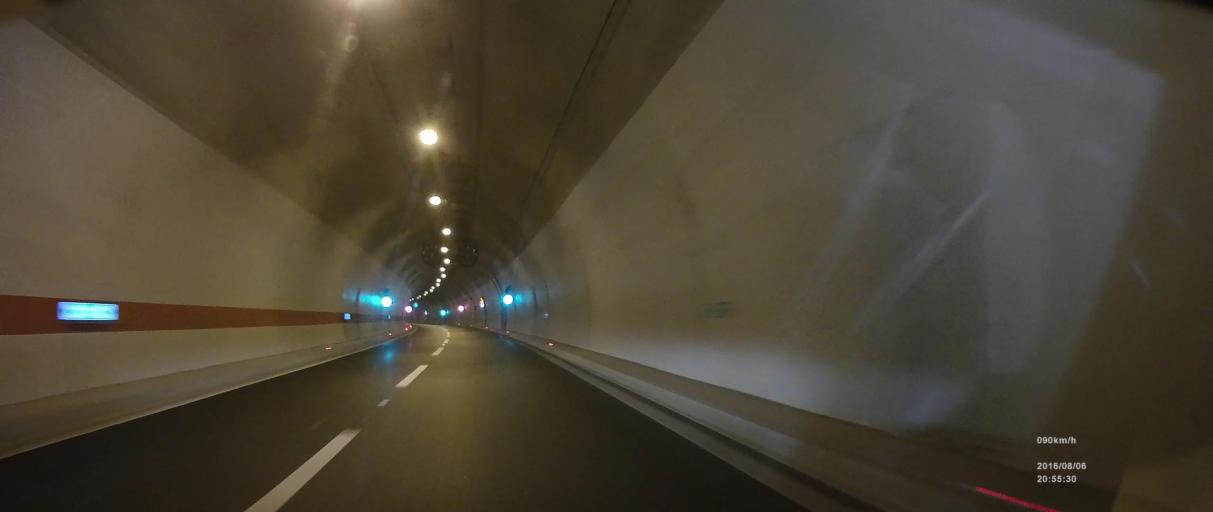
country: BA
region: Federation of Bosnia and Herzegovina
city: Vitina
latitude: 43.1622
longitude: 17.4709
